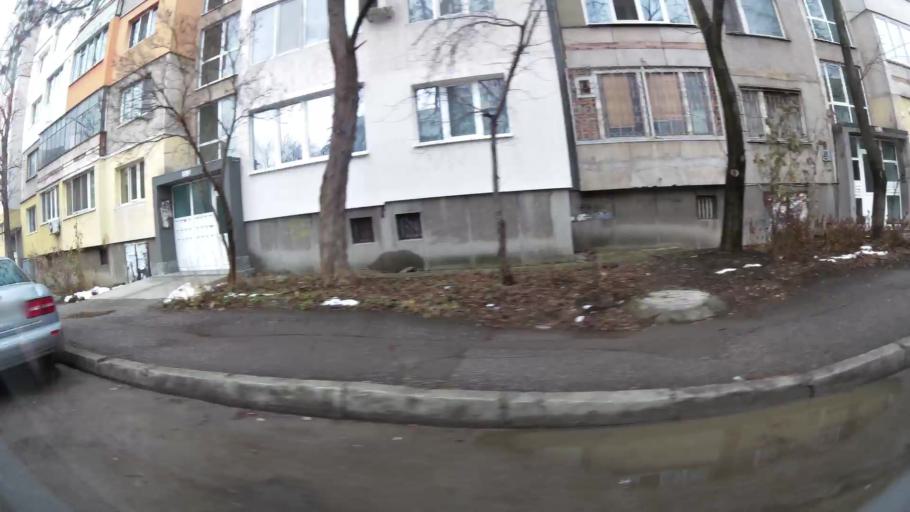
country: BG
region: Sofiya
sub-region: Obshtina Bozhurishte
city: Bozhurishte
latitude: 42.7284
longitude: 23.2519
